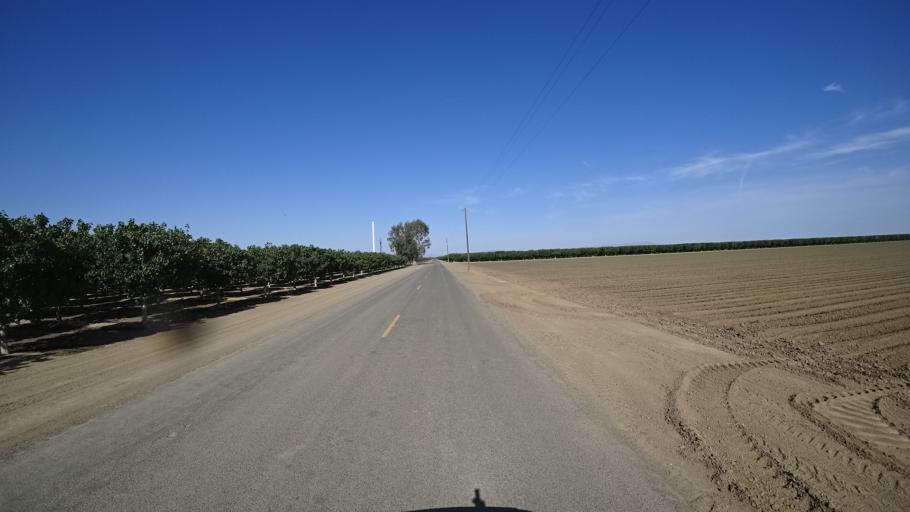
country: US
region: California
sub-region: Kings County
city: Kettleman City
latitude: 36.1089
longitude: -120.0198
